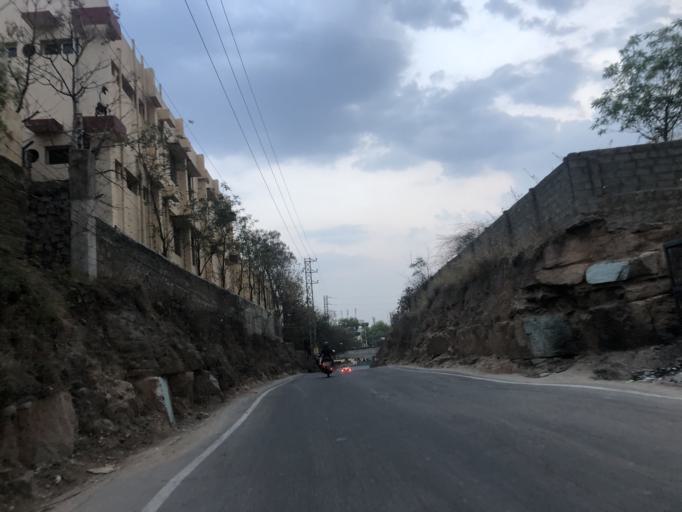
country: IN
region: Telangana
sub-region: Hyderabad
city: Hyderabad
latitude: 17.4087
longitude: 78.4020
